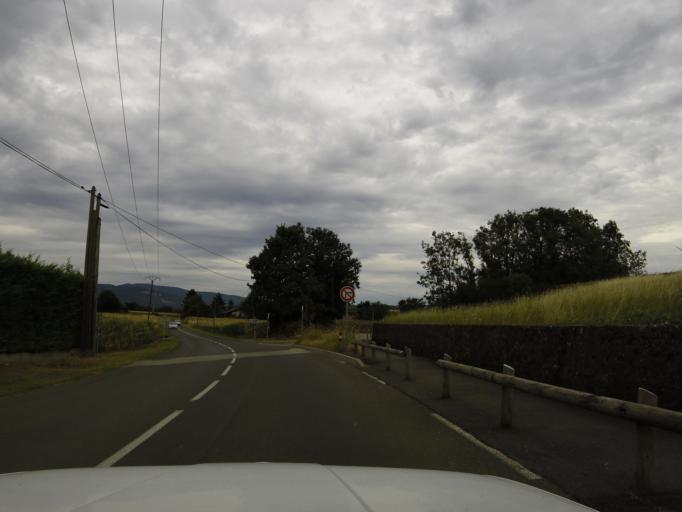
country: FR
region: Rhone-Alpes
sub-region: Departement de l'Ain
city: Chazey-sur-Ain
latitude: 45.8862
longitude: 5.2836
